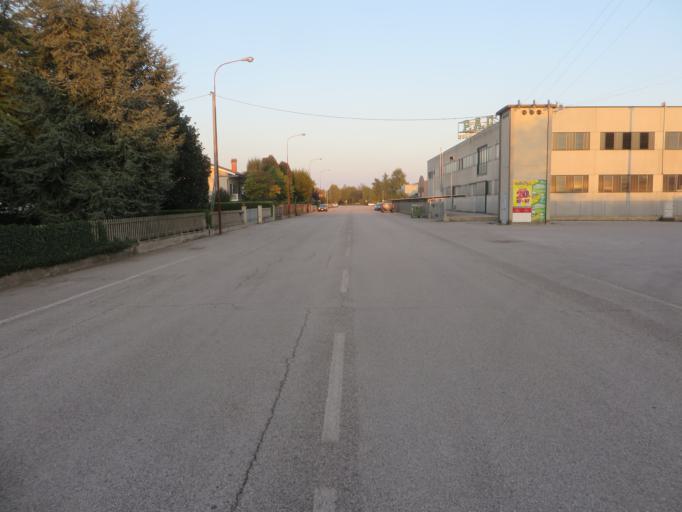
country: IT
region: Veneto
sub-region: Provincia di Verona
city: San Pietro di Morubio
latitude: 45.2265
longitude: 11.2408
